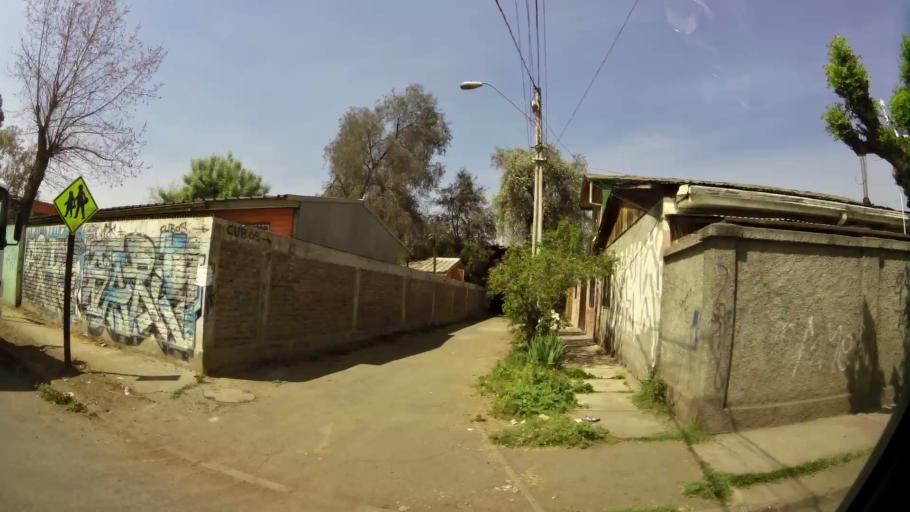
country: CL
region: Santiago Metropolitan
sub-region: Provincia de Santiago
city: Lo Prado
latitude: -33.4126
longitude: -70.7188
